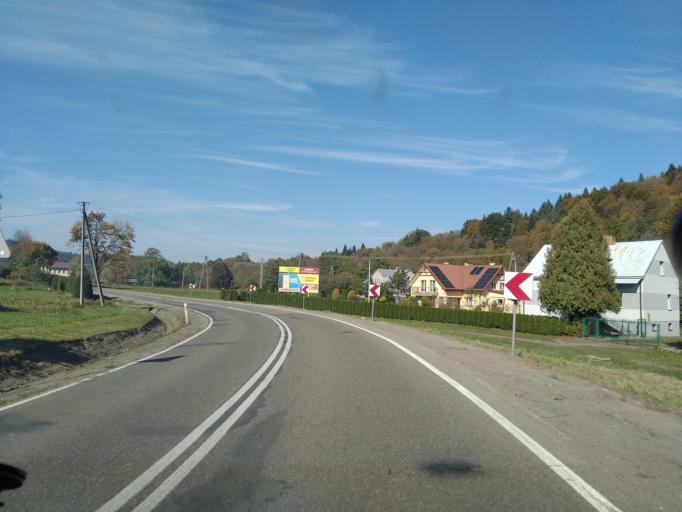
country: PL
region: Subcarpathian Voivodeship
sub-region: Powiat leski
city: Baligrod
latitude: 49.3873
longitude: 22.2879
